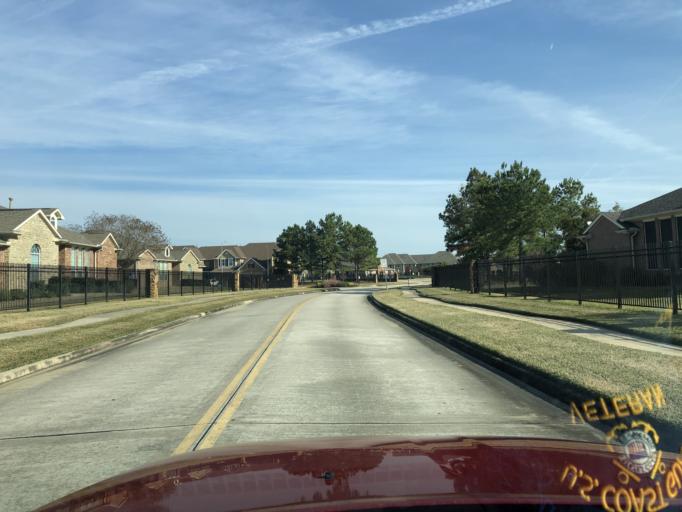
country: US
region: Texas
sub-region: Harris County
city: Tomball
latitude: 30.0374
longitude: -95.5546
